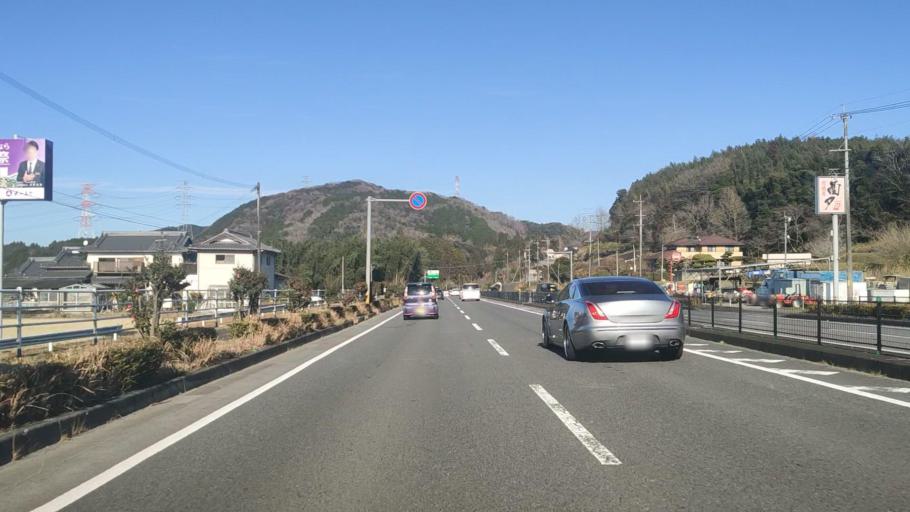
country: JP
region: Oita
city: Oita
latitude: 33.1057
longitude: 131.6543
